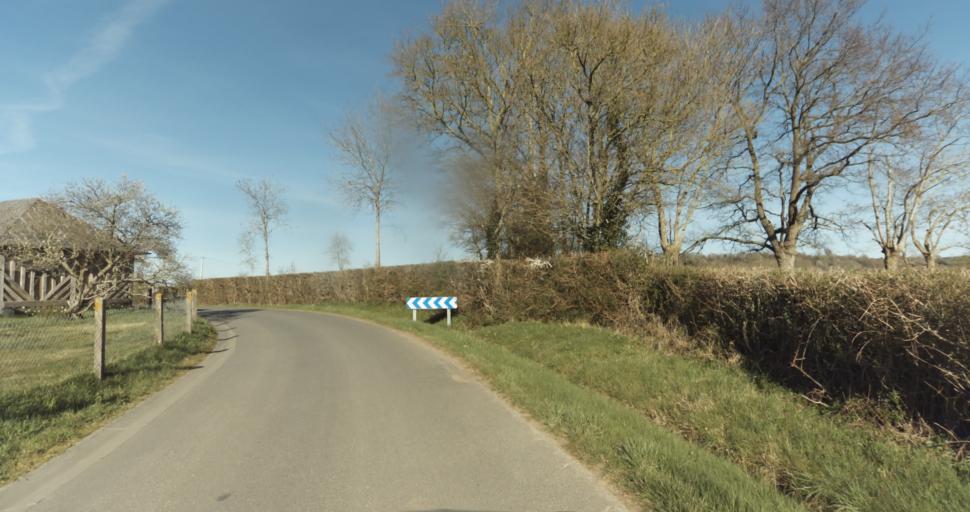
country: FR
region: Lower Normandy
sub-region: Departement du Calvados
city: Saint-Pierre-sur-Dives
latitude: 49.0301
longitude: 0.0578
